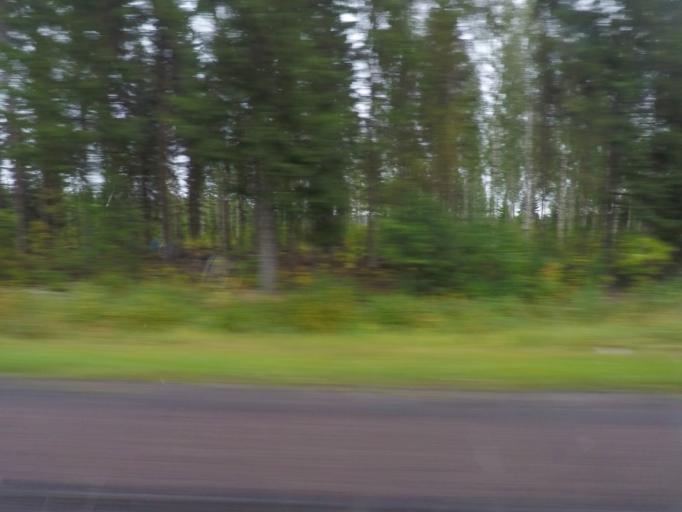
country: FI
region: Northern Savo
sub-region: Varkaus
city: Leppaevirta
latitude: 62.4591
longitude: 27.7861
